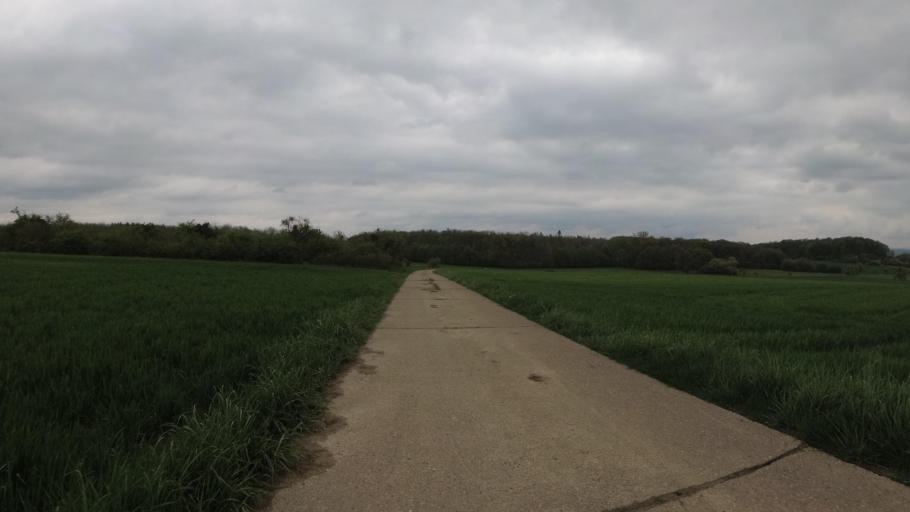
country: DE
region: Saarland
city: Merzig
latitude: 49.4006
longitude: 6.5797
